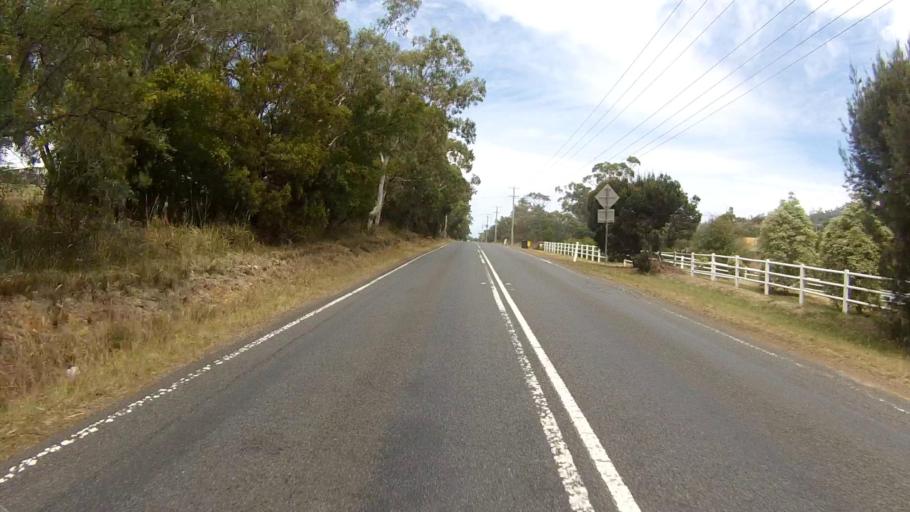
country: AU
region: Tasmania
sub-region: Clarence
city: Acton Park
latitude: -42.8693
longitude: 147.4839
